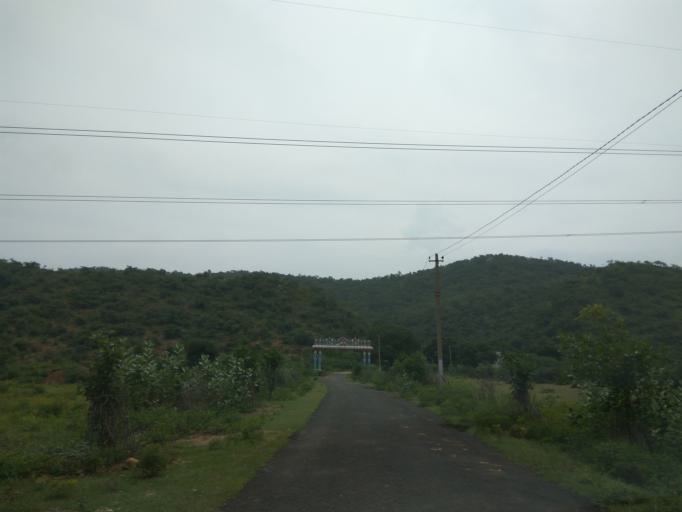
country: IN
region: Andhra Pradesh
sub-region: Prakasam
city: Cumbum
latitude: 15.4443
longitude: 79.0812
